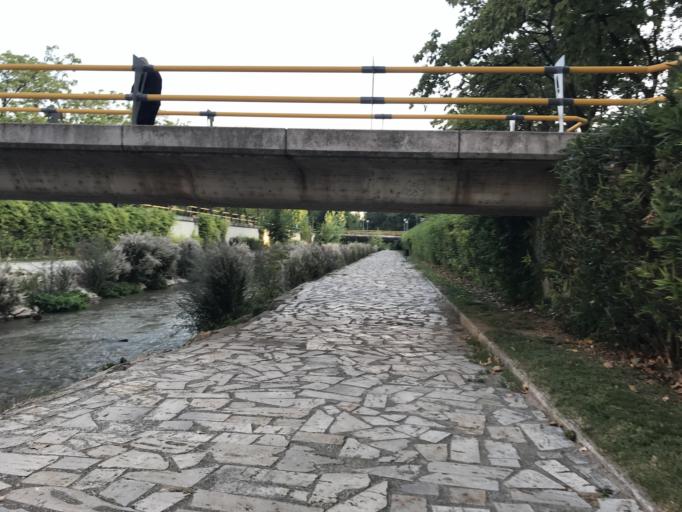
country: ES
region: Castille and Leon
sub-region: Provincia de Valladolid
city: Valladolid
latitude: 41.6555
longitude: -4.7113
